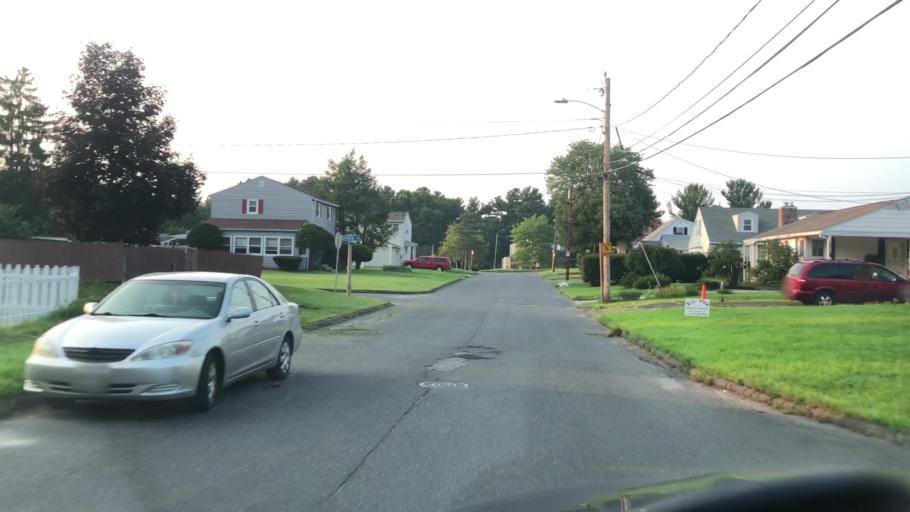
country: US
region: Massachusetts
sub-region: Hampden County
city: Holyoke
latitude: 42.1963
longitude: -72.6273
